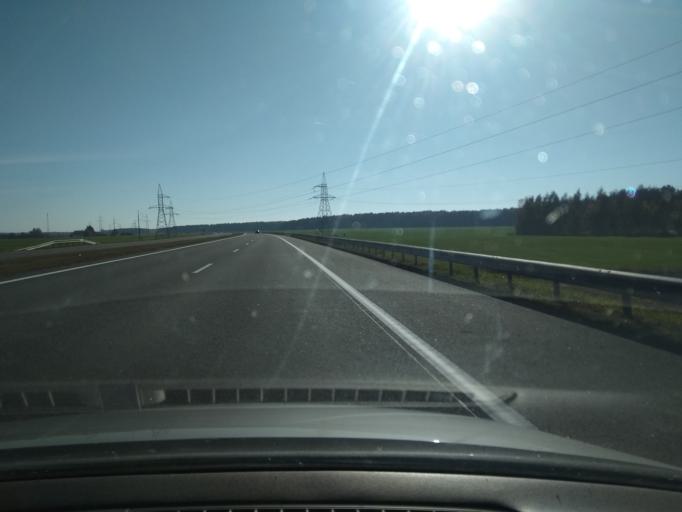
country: BY
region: Brest
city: Baranovichi
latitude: 53.1043
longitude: 25.8881
